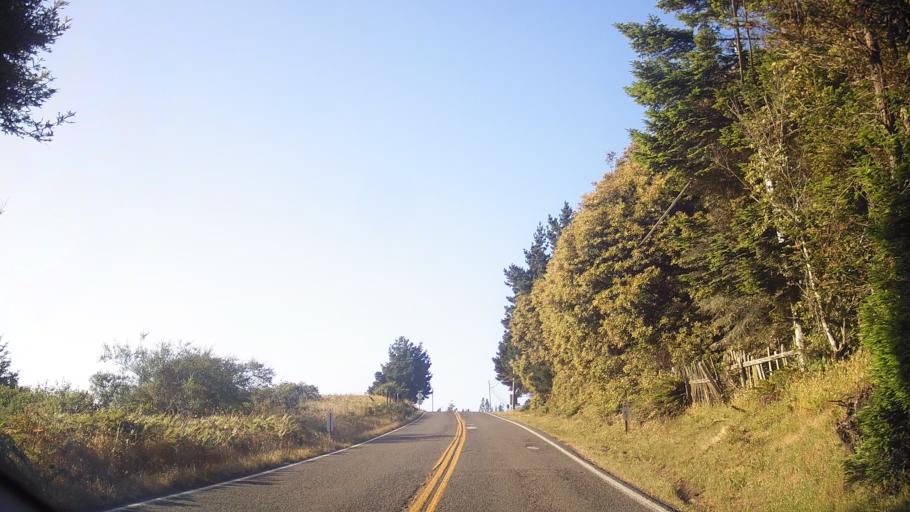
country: US
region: California
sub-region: Mendocino County
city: Fort Bragg
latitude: 39.5099
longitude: -123.7648
